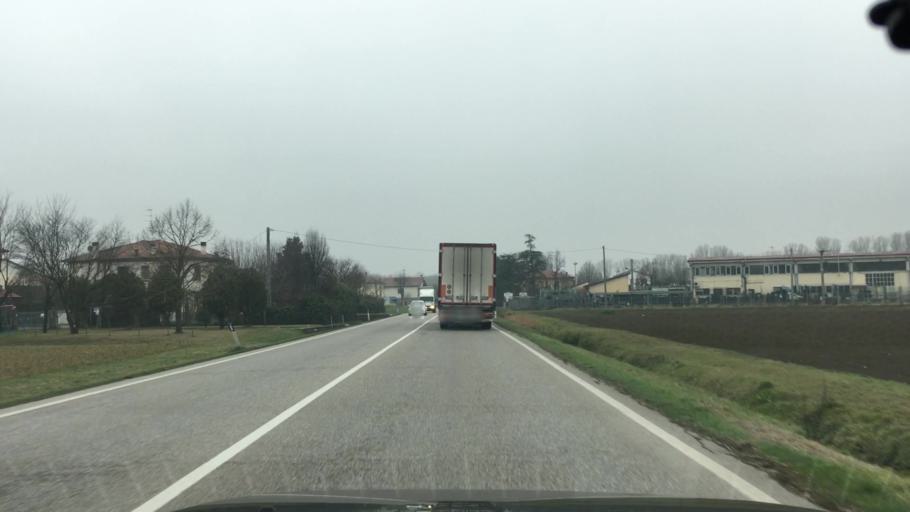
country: IT
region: Emilia-Romagna
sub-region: Provincia di Bologna
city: San Giovanni in Persiceto
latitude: 44.6269
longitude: 11.2128
